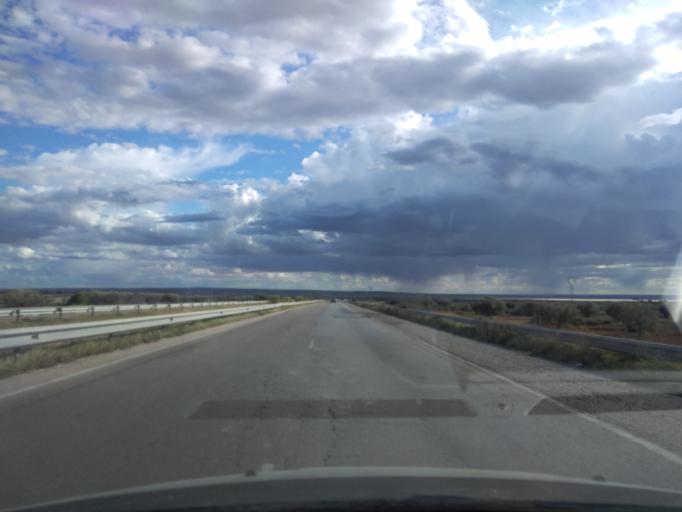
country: TN
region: Al Munastir
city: Manzil Kamil
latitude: 35.5182
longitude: 10.6265
